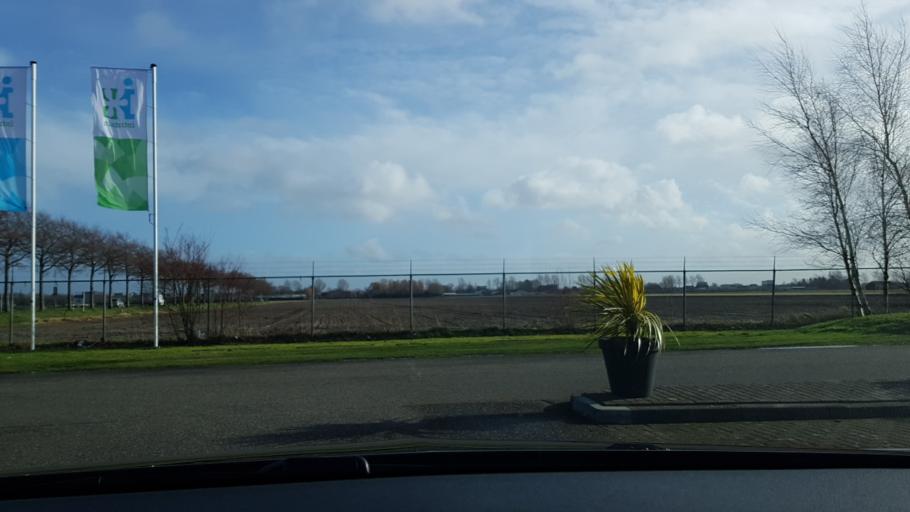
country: NL
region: North Holland
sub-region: Gemeente Heemstede
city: Heemstede
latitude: 52.3305
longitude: 4.6323
